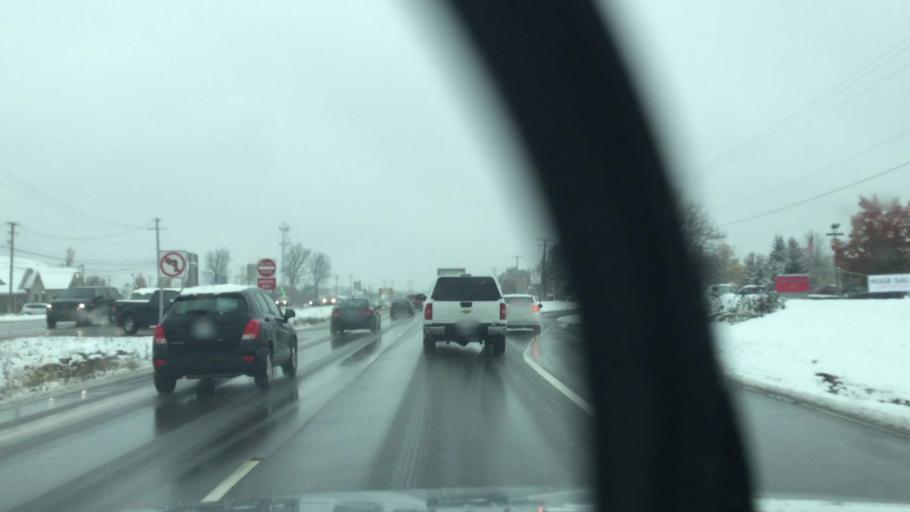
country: US
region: Michigan
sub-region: Oakland County
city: Lake Orion
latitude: 42.7611
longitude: -83.2436
